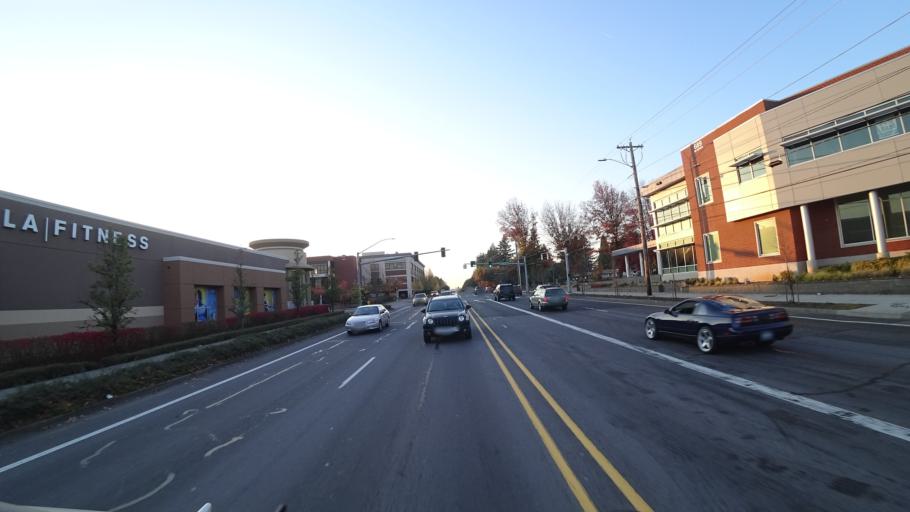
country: US
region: Oregon
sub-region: Multnomah County
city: Gresham
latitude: 45.5109
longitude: -122.4386
